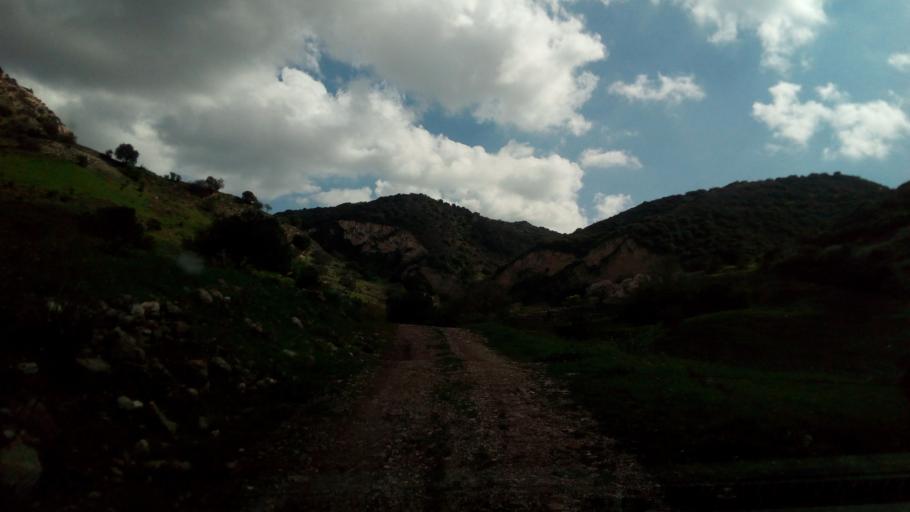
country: CY
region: Pafos
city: Mesogi
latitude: 34.8049
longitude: 32.5403
